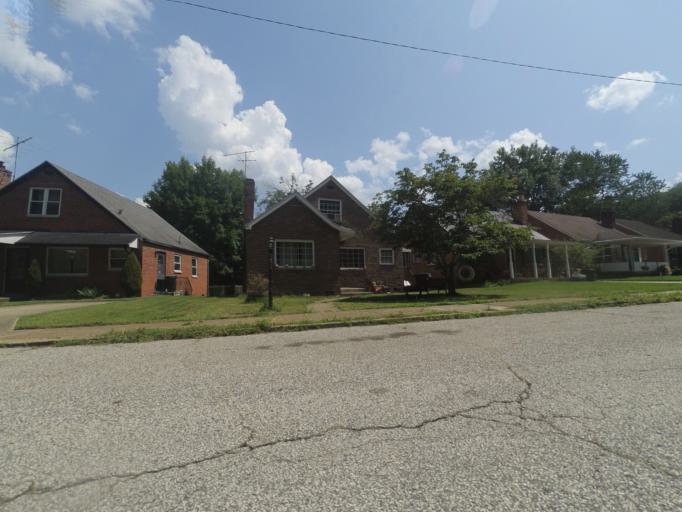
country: US
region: West Virginia
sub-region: Cabell County
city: Huntington
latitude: 38.3987
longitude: -82.4282
